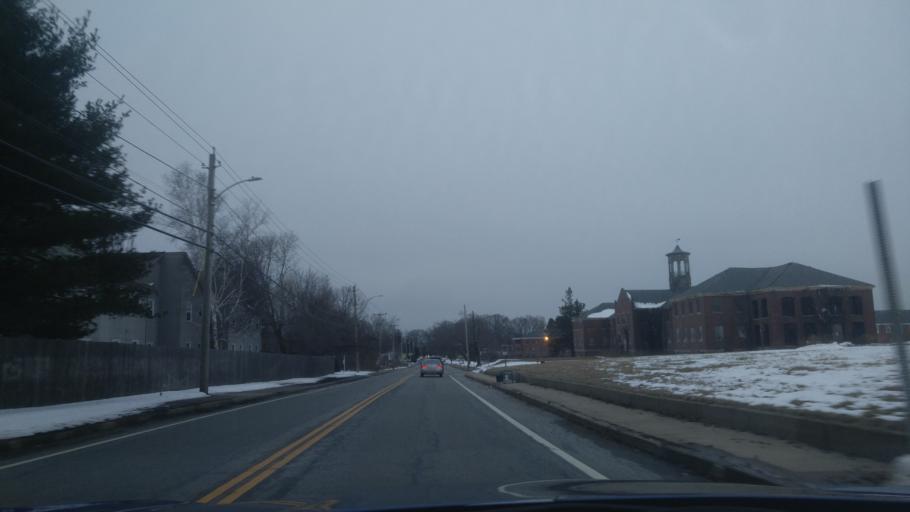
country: US
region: Rhode Island
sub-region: Providence County
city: Cranston
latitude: 41.7393
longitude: -71.4625
